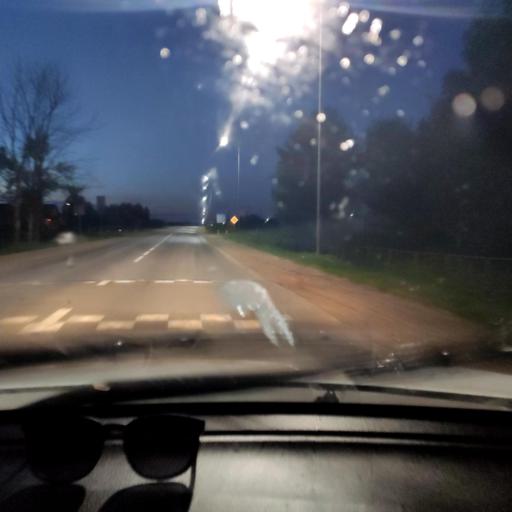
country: RU
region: Tatarstan
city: Rybnaya Sloboda
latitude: 55.4292
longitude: 49.8902
